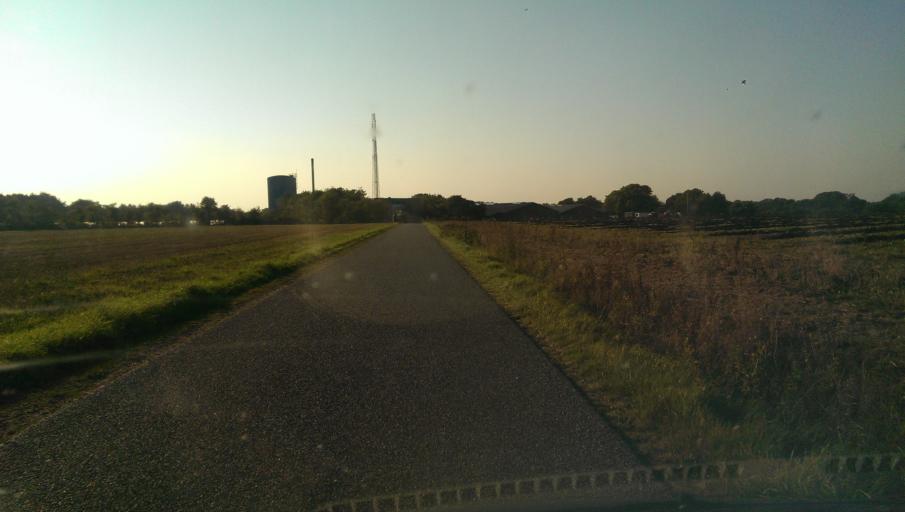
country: DK
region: South Denmark
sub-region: Esbjerg Kommune
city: Bramming
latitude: 55.4768
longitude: 8.8081
